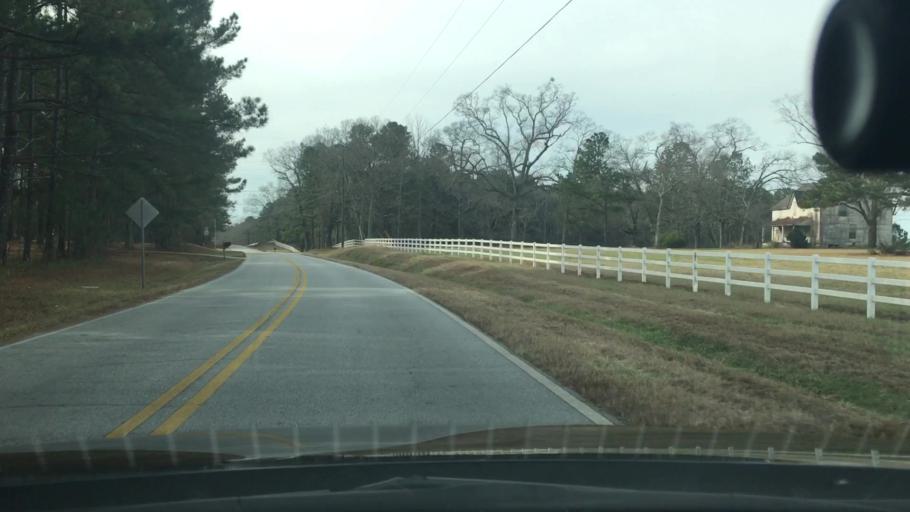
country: US
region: Georgia
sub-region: Spalding County
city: Experiment
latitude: 33.2820
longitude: -84.4016
